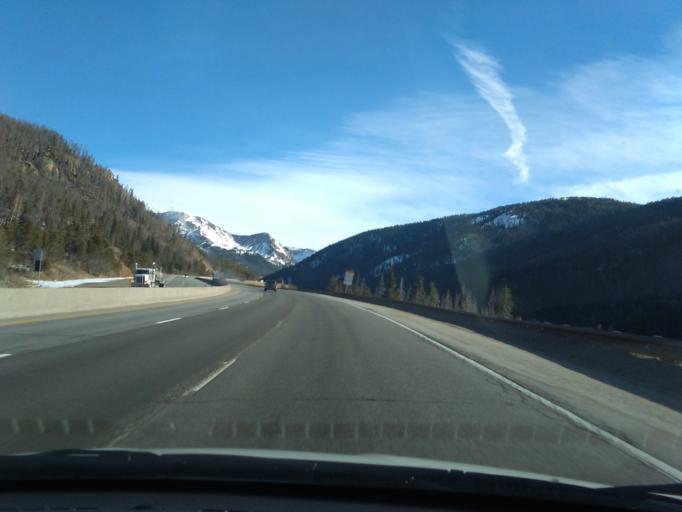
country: US
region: Colorado
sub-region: Summit County
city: Keystone
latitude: 39.6574
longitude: -105.9926
